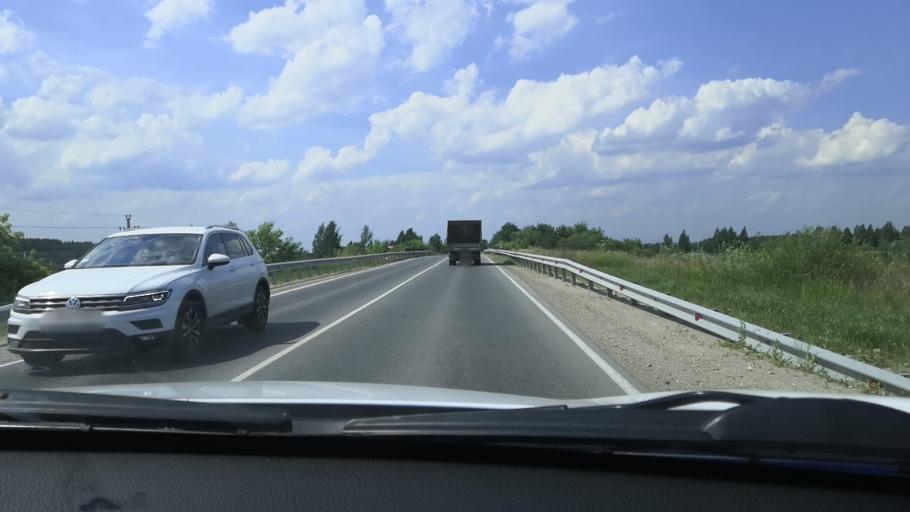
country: RU
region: Rjazan
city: Murmino
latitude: 54.6330
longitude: 39.9502
